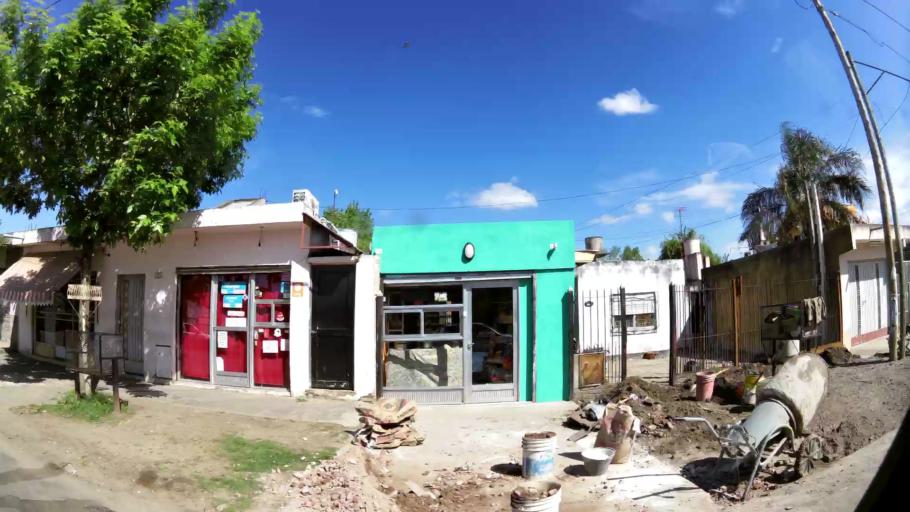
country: AR
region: Buenos Aires
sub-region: Partido de Quilmes
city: Quilmes
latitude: -34.8001
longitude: -58.2533
